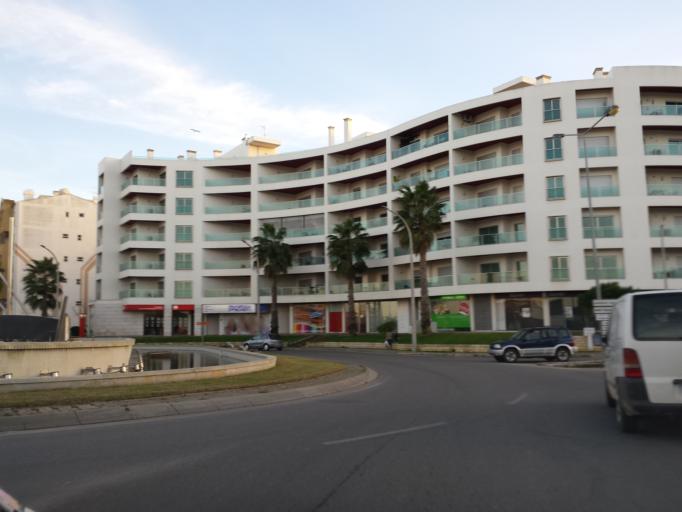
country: PT
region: Faro
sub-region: Lagos
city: Lagos
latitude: 37.1116
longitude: -8.6813
